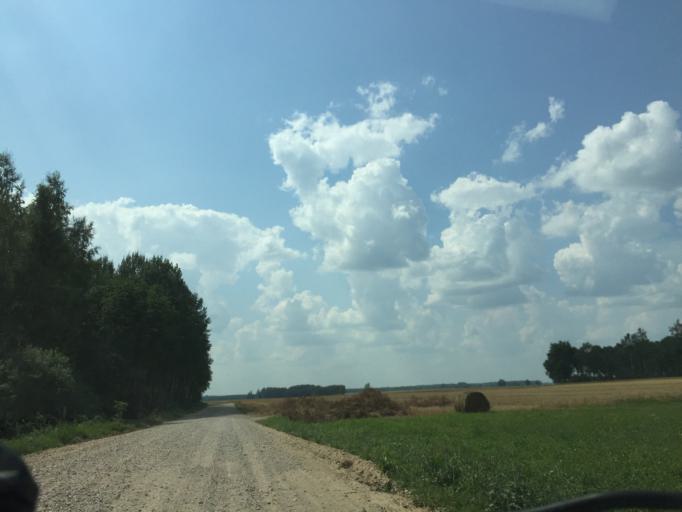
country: LT
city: Zagare
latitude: 56.3922
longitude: 23.1983
